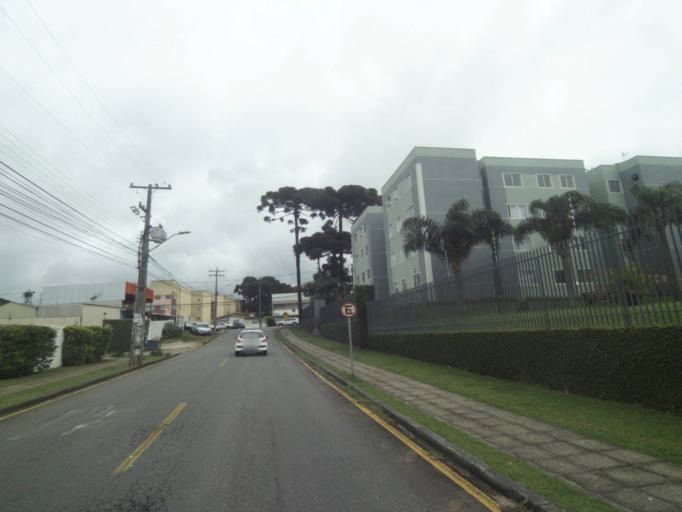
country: BR
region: Parana
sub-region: Curitiba
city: Curitiba
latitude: -25.4967
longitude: -49.3024
